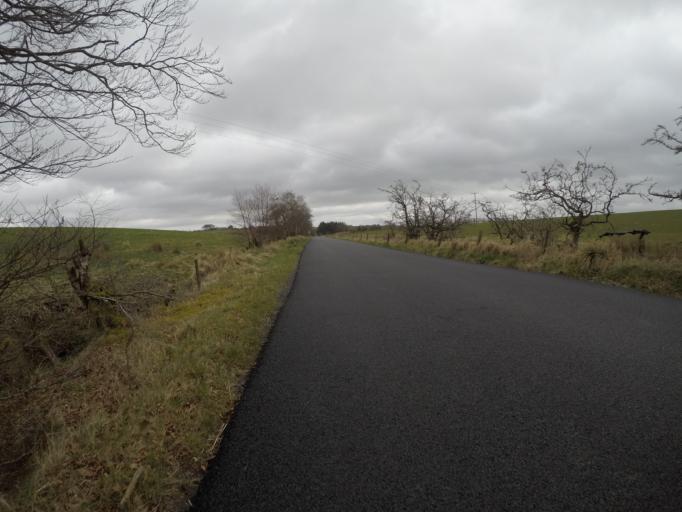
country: GB
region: Scotland
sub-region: East Ayrshire
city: Stewarton
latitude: 55.6811
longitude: -4.4586
